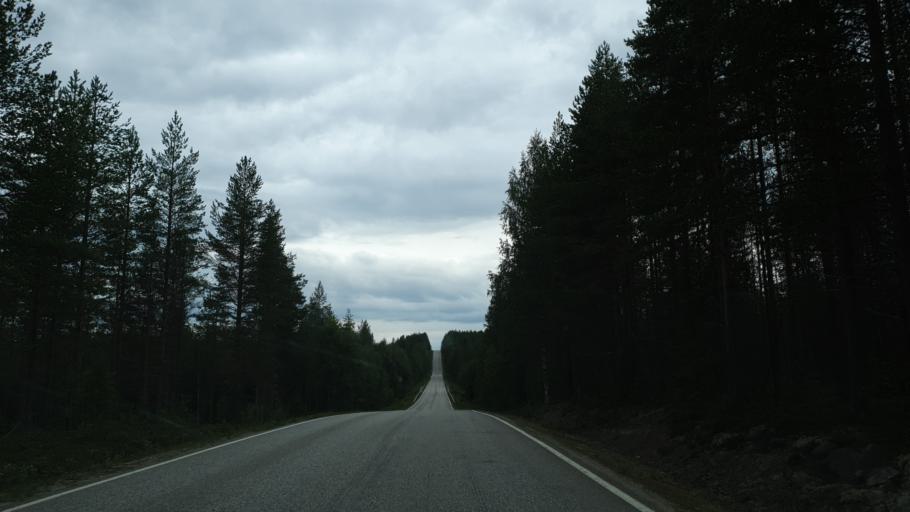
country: FI
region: Kainuu
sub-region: Kehys-Kainuu
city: Kuhmo
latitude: 64.3086
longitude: 29.4273
